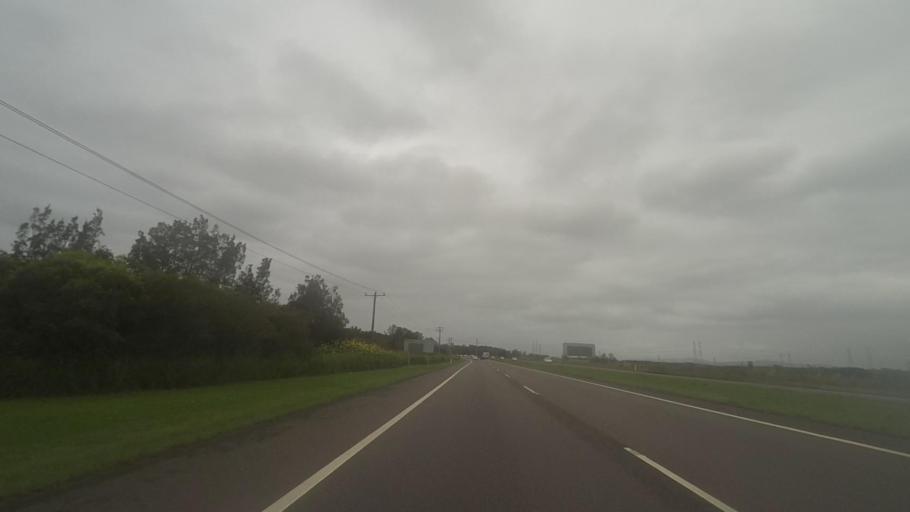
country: AU
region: New South Wales
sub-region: Port Stephens Shire
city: Raymond Terrace
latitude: -32.8031
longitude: 151.7143
